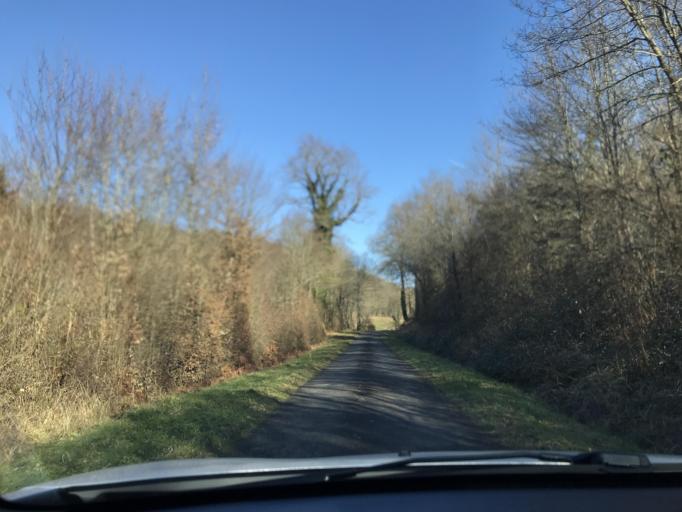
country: FR
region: Poitou-Charentes
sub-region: Departement de la Charente
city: Saint-Claud
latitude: 45.8509
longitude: 0.5187
